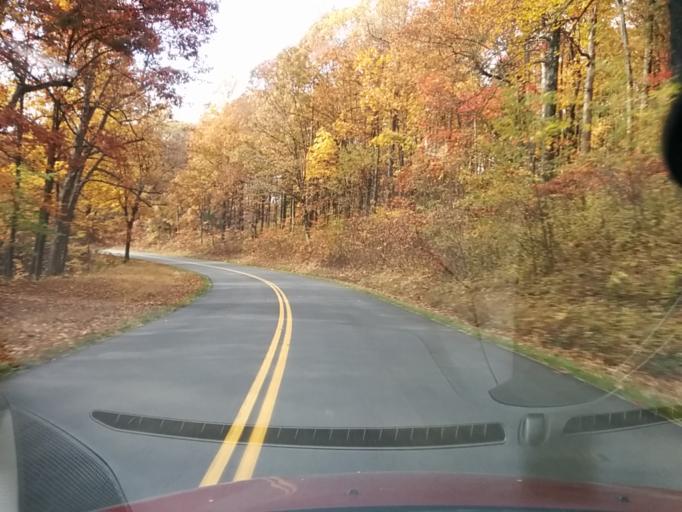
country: US
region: Virginia
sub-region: Augusta County
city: Stuarts Draft
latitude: 37.8924
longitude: -79.0187
